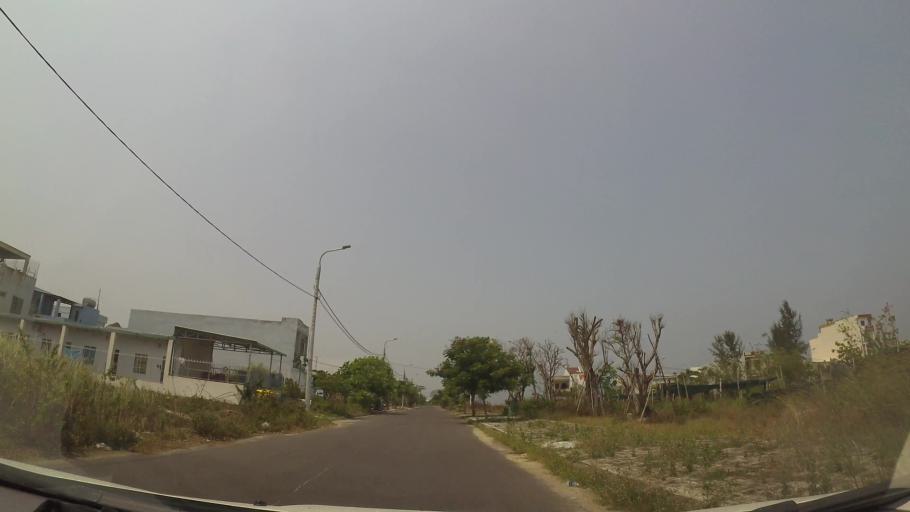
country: VN
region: Da Nang
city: Ngu Hanh Son
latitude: 15.9875
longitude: 108.2698
